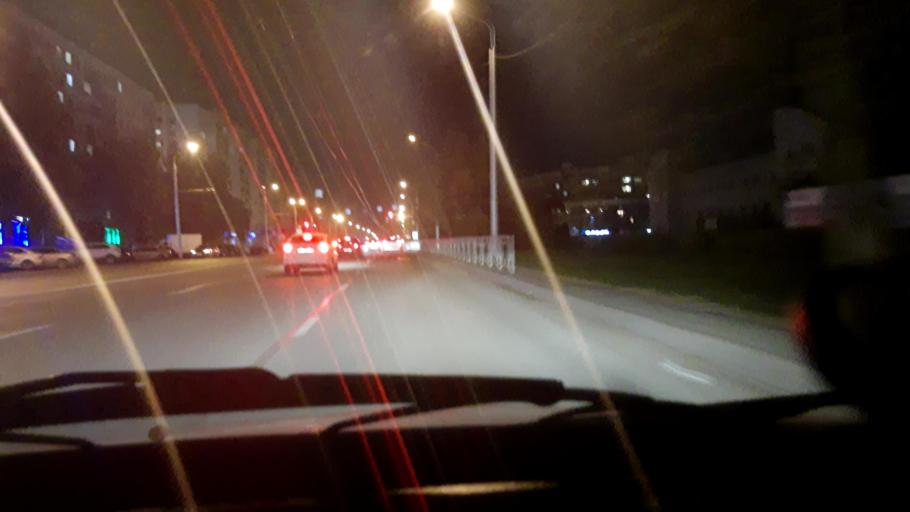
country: RU
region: Bashkortostan
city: Ufa
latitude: 54.7659
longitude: 56.0270
